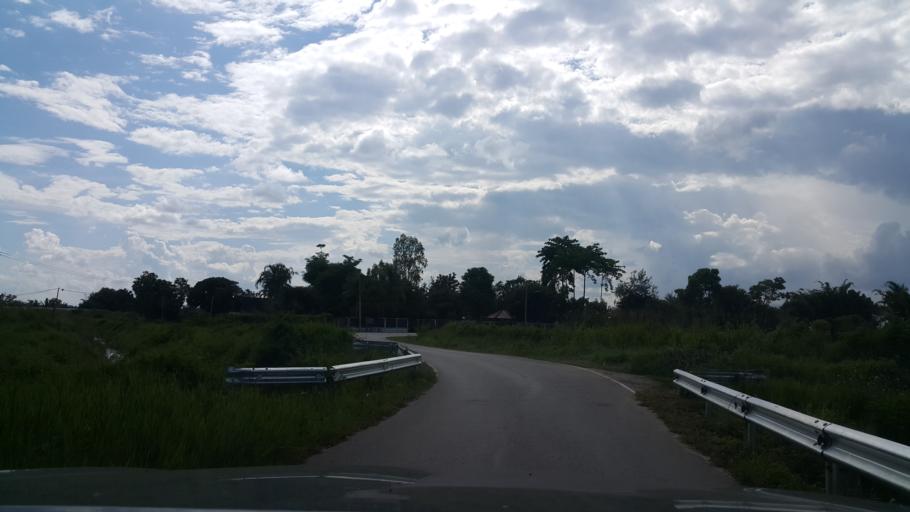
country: TH
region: Chiang Mai
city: San Kamphaeng
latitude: 18.7106
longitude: 99.1551
